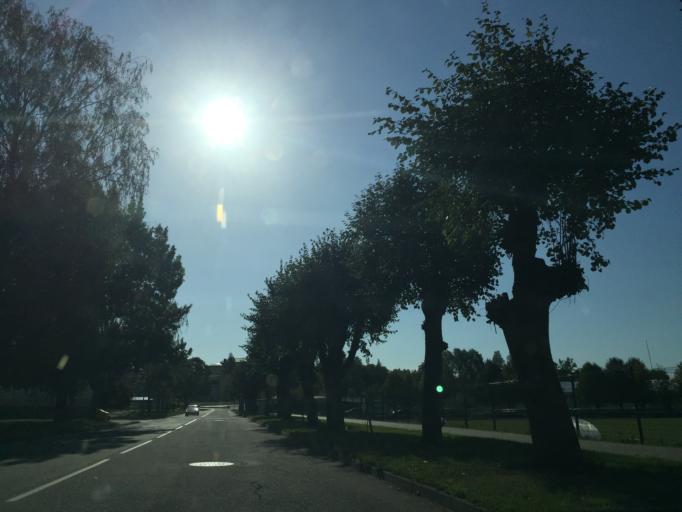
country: LV
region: Limbazu Rajons
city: Limbazi
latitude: 57.5094
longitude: 24.7087
